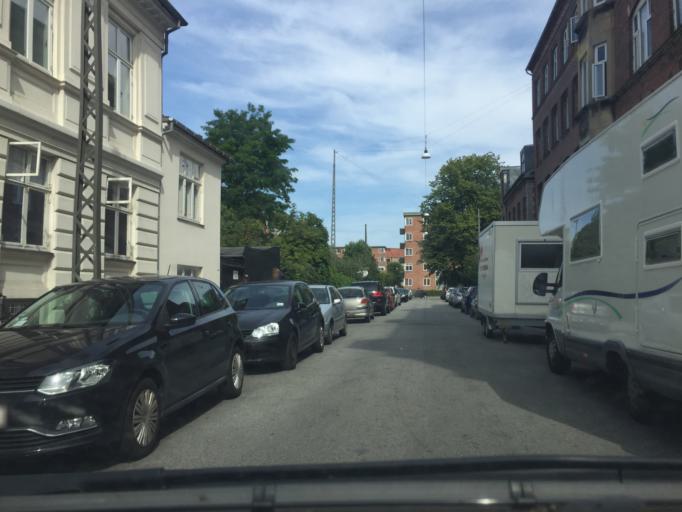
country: DK
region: Capital Region
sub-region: Kobenhavn
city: Christianshavn
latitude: 55.6614
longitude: 12.6040
